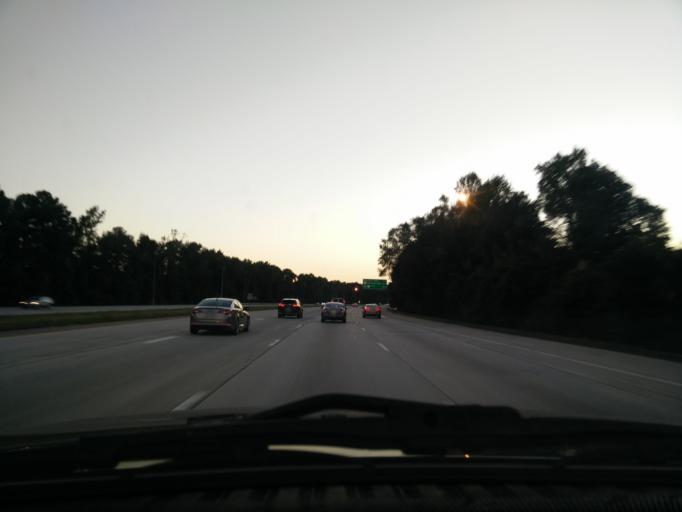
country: US
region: Virginia
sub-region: City of Chesapeake
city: Chesapeake
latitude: 36.8026
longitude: -76.1989
